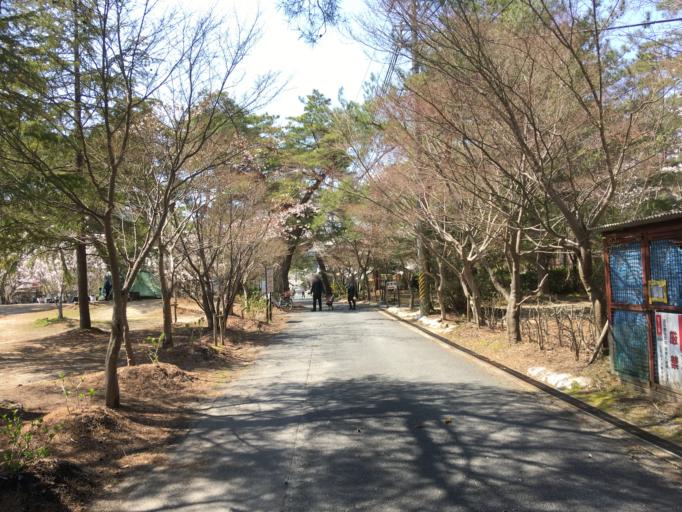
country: JP
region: Kyoto
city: Tanabe
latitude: 34.7627
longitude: 135.7142
